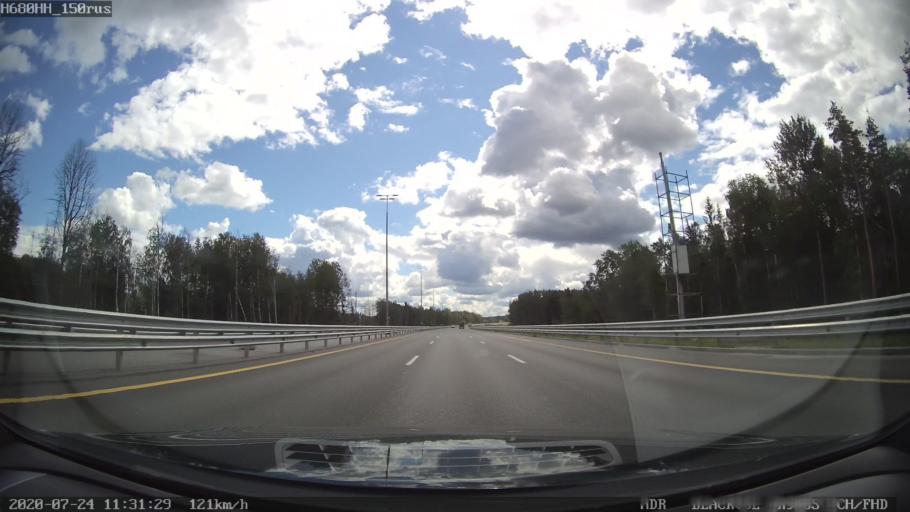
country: RU
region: Leningrad
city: Krasnyy Bor
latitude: 59.6556
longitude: 30.6382
